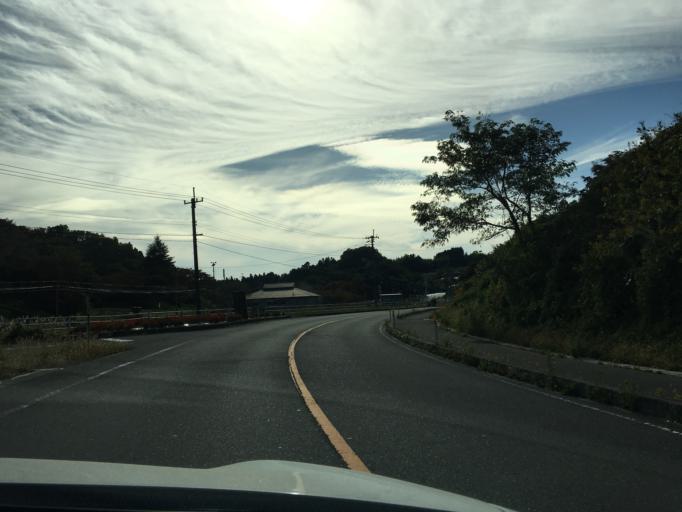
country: JP
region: Fukushima
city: Miharu
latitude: 37.4125
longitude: 140.4616
